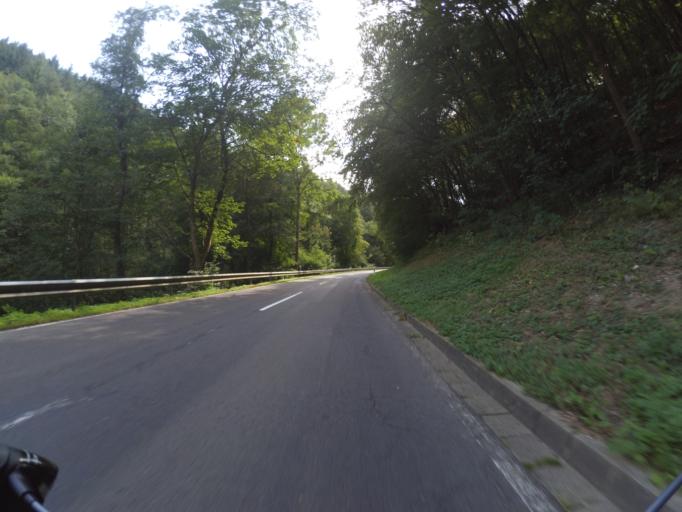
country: DE
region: Rheinland-Pfalz
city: Heidenburg
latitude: 49.8008
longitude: 6.9019
